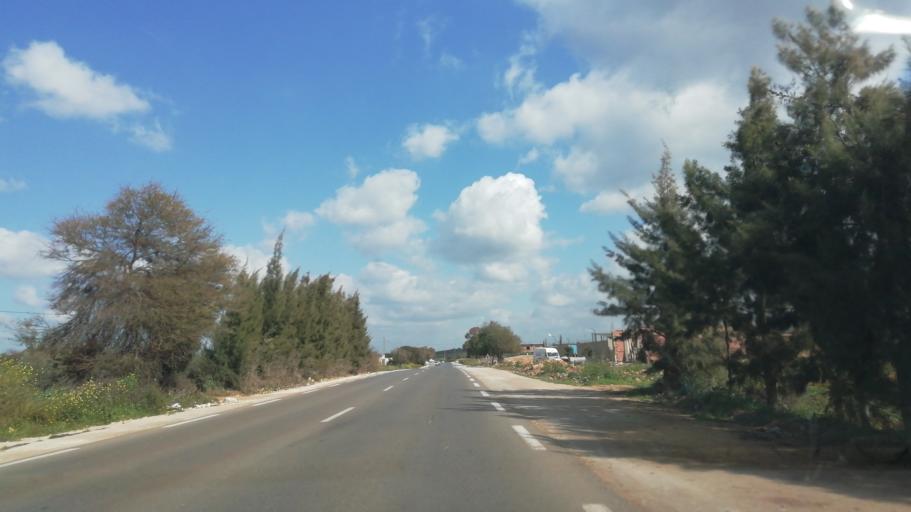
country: DZ
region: Relizane
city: Relizane
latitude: 35.7142
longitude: 0.2890
